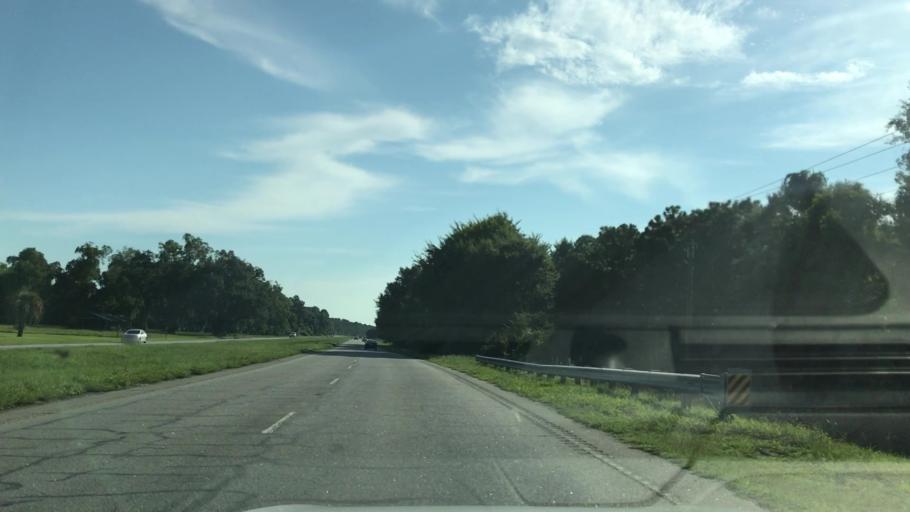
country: US
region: South Carolina
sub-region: Charleston County
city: Awendaw
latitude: 33.0552
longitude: -79.5466
